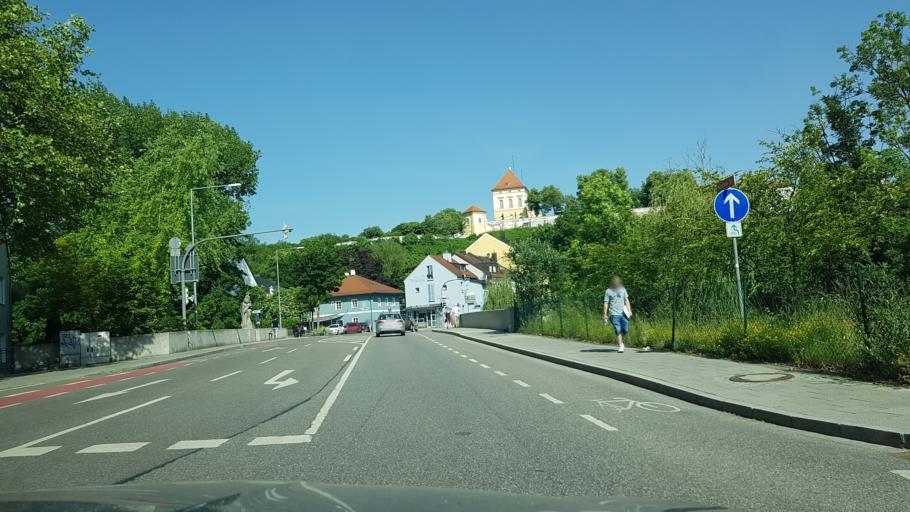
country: DE
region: Bavaria
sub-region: Upper Bavaria
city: Dachau
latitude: 48.2564
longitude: 11.4369
